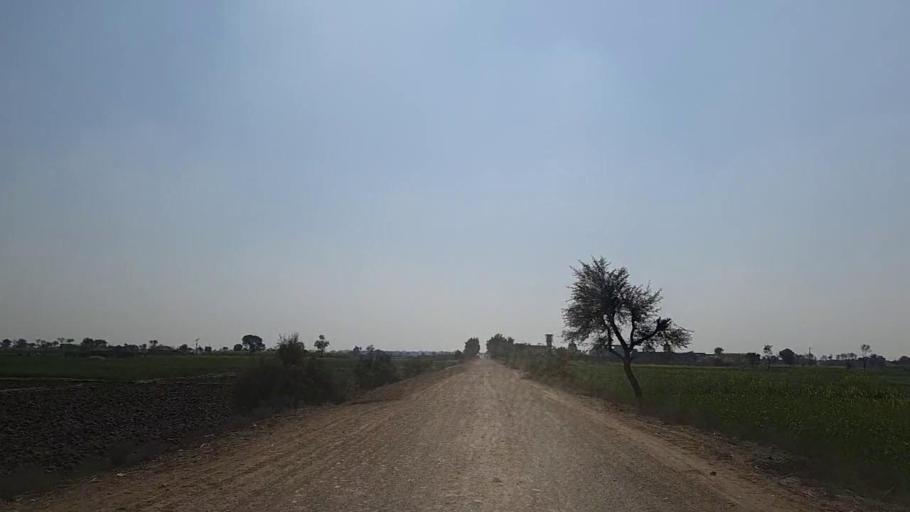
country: PK
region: Sindh
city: Daur
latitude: 26.4597
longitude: 68.2709
